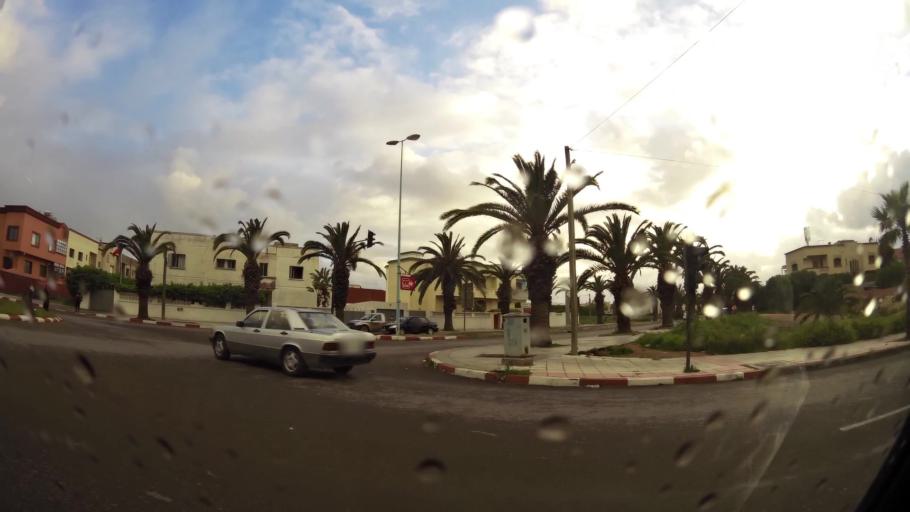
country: MA
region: Doukkala-Abda
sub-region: El-Jadida
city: El Jadida
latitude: 33.2418
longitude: -8.5035
